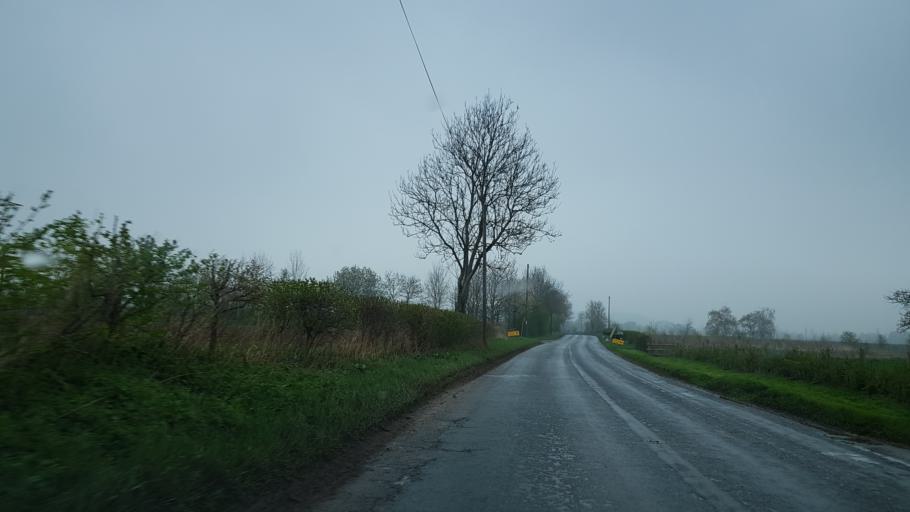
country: GB
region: England
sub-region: Herefordshire
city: Ledbury
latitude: 52.0785
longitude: -2.4567
